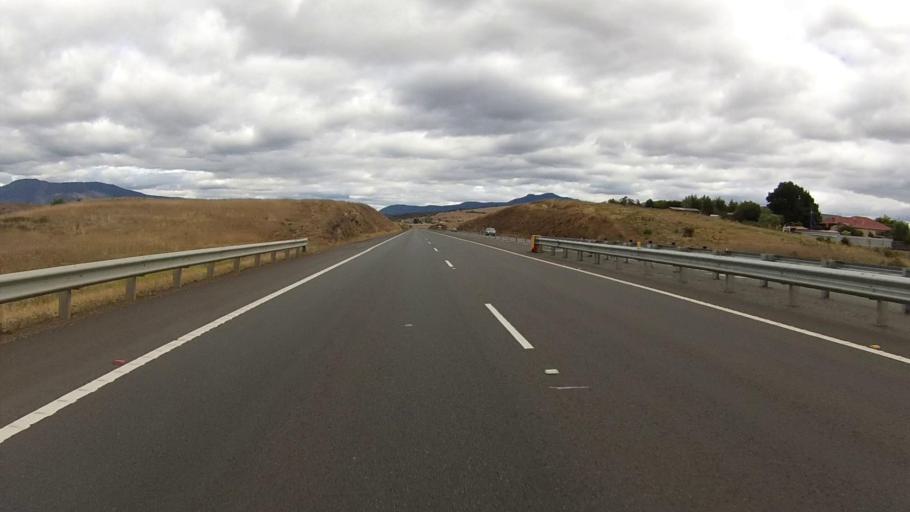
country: AU
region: Tasmania
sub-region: Brighton
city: Bridgewater
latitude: -42.7054
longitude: 147.2642
